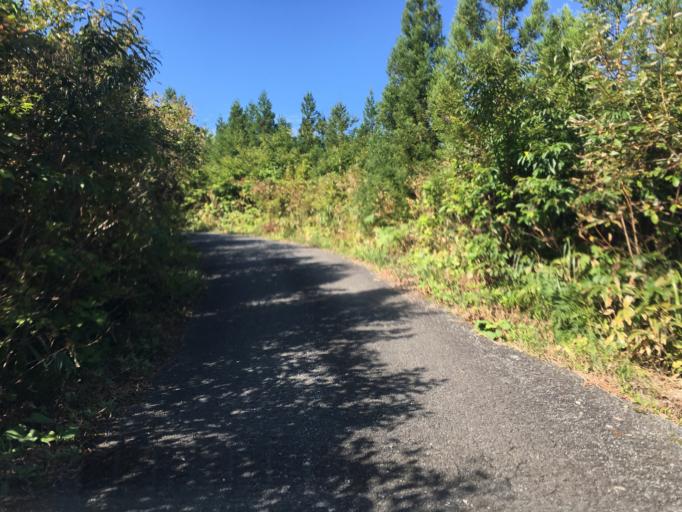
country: JP
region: Yamagata
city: Yonezawa
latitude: 37.8156
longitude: 140.2494
